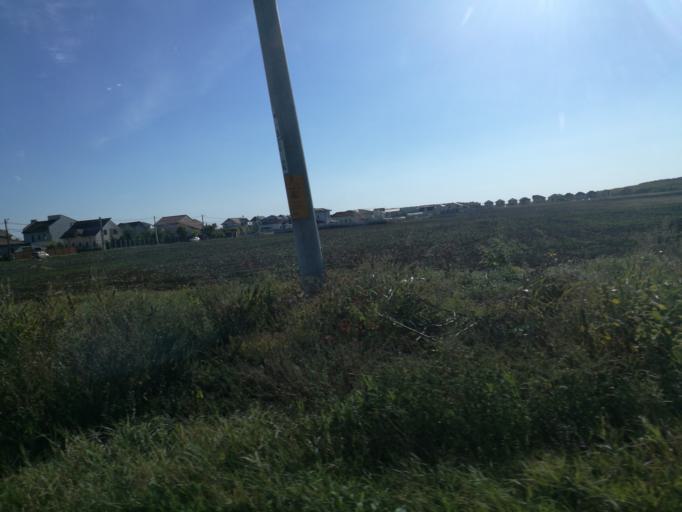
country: RO
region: Ilfov
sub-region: Comuna Dragomiresti-Vale
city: Dragomiresti-Vale
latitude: 44.4660
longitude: 25.9275
